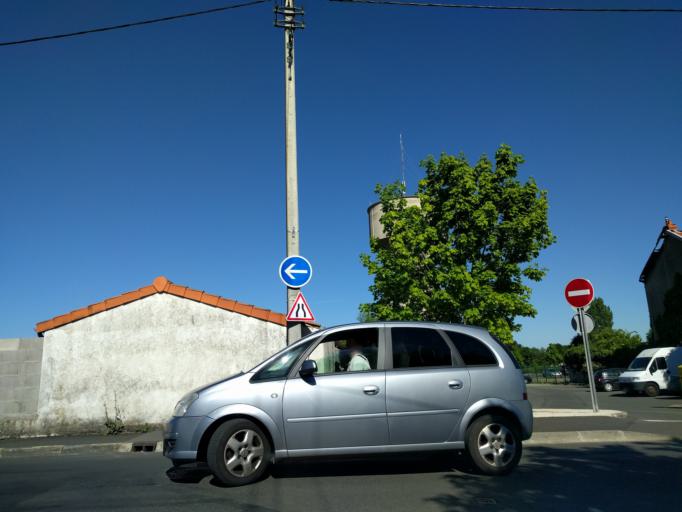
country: FR
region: Poitou-Charentes
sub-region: Departement des Deux-Sevres
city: Niort
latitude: 46.3333
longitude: -0.4586
